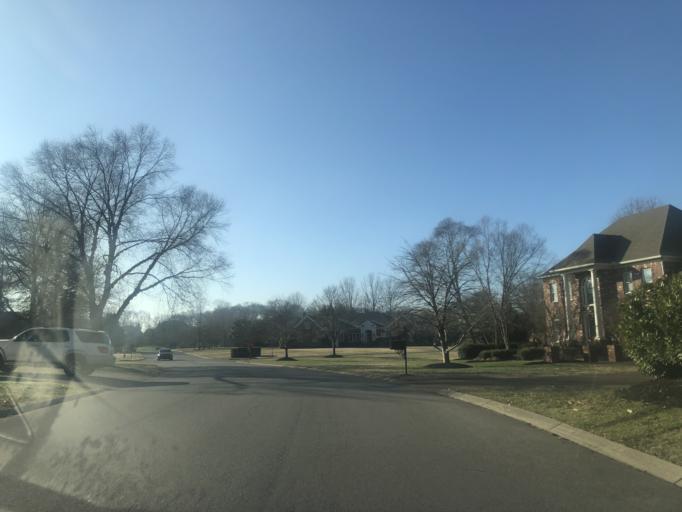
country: US
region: Tennessee
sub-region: Williamson County
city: Brentwood Estates
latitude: 35.9909
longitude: -86.7251
